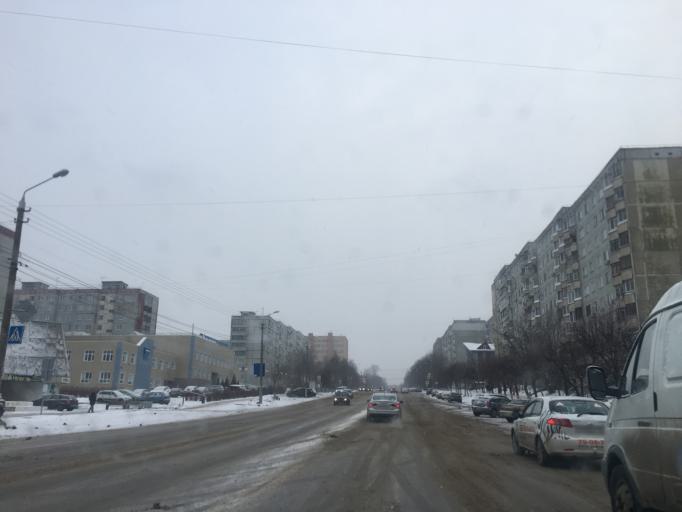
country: RU
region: Tula
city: Tula
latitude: 54.1958
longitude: 37.5906
